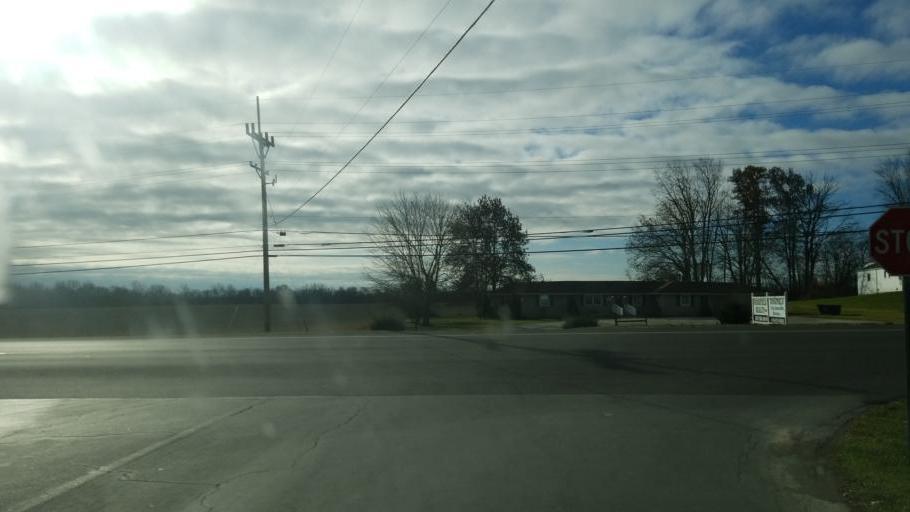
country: US
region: Ohio
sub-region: Hardin County
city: Kenton
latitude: 40.6449
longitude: -83.5905
